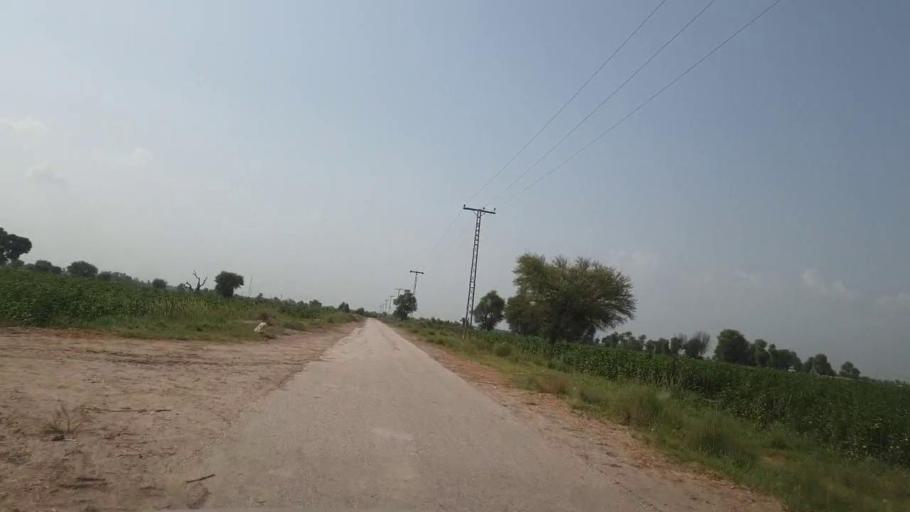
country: PK
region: Sindh
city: Pano Aqil
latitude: 27.7865
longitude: 69.1569
